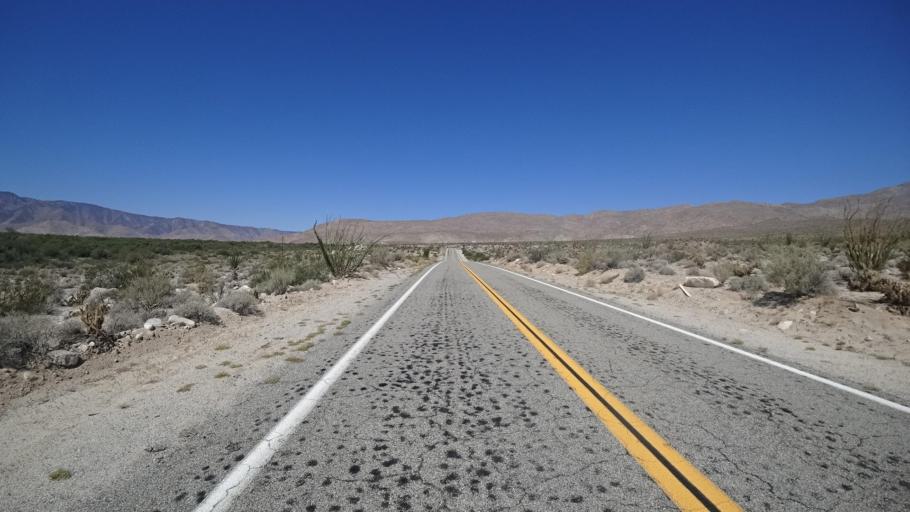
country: US
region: California
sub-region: San Diego County
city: Pine Valley
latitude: 32.9733
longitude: -116.3429
